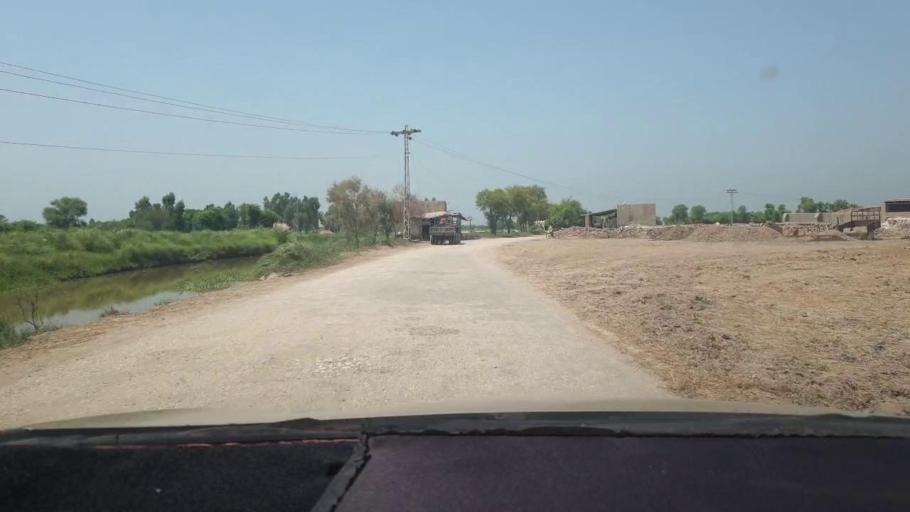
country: PK
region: Sindh
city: Miro Khan
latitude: 27.6704
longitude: 68.0607
